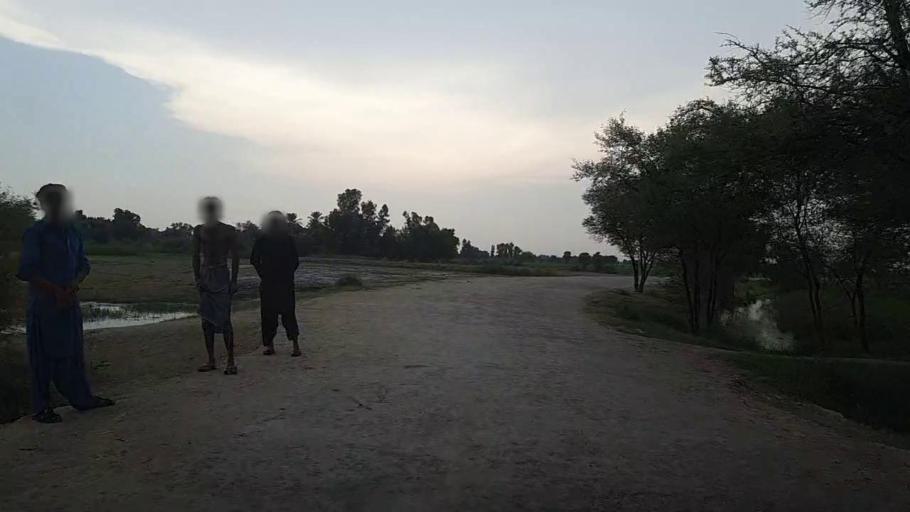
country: PK
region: Sindh
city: Khanpur
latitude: 27.8379
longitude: 69.4705
